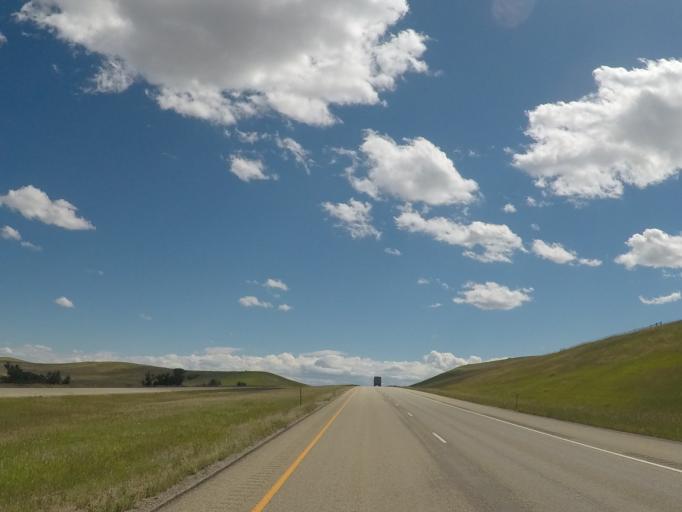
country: US
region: Montana
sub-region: Big Horn County
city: Crow Agency
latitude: 45.2438
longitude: -107.3562
